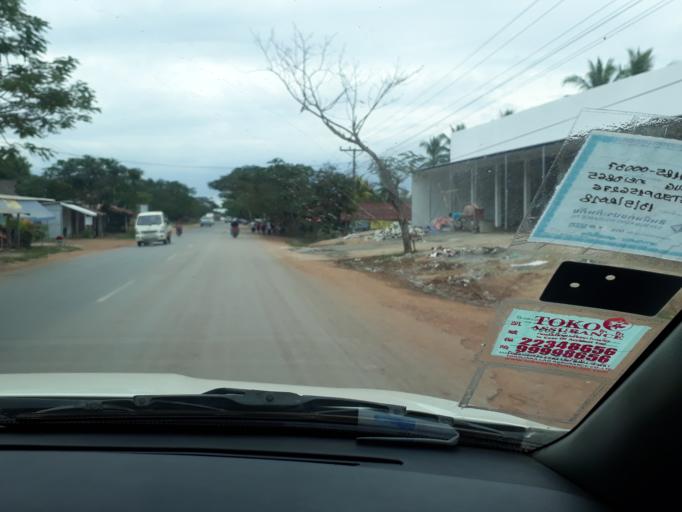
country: LA
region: Vientiane
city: Muang Phon-Hong
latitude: 18.3291
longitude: 102.4442
